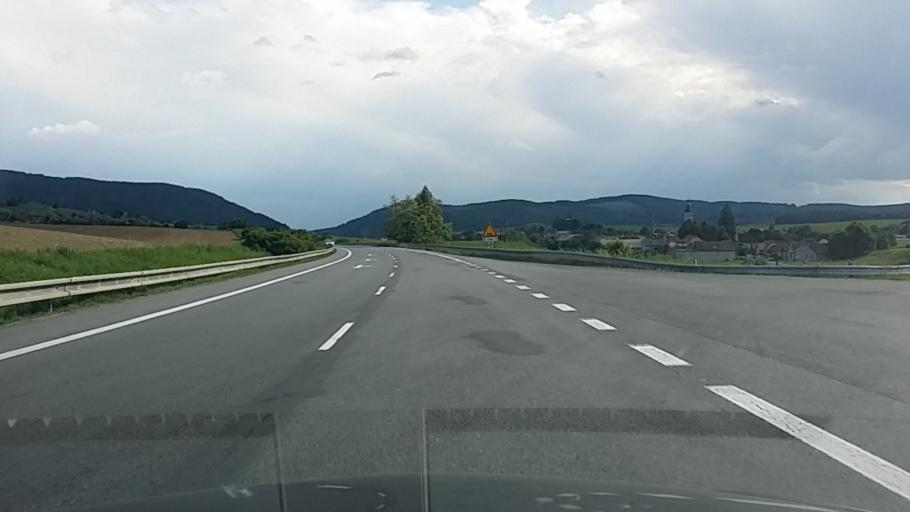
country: SK
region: Banskobystricky
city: Krupina
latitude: 48.4414
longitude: 19.0964
